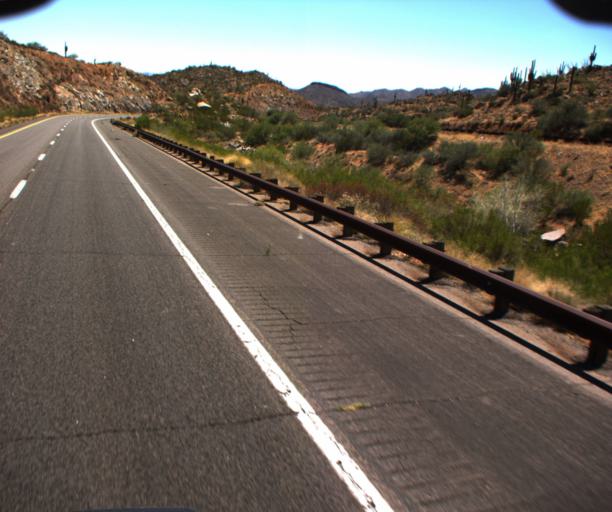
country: US
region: Arizona
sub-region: Gila County
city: Tonto Basin
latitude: 33.8205
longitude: -111.4772
